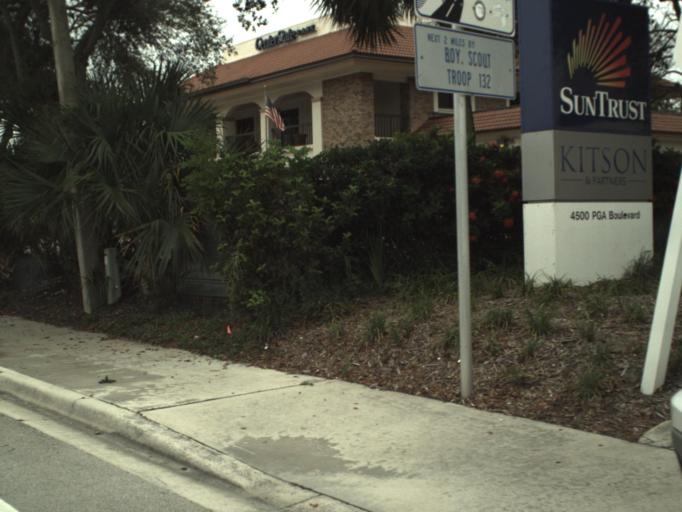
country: US
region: Florida
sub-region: Palm Beach County
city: North Palm Beach
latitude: 26.8375
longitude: -80.1054
